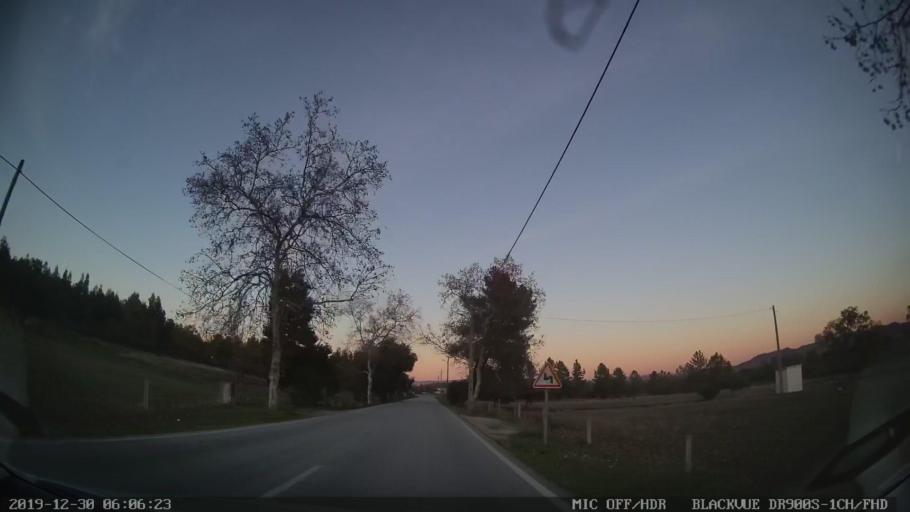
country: PT
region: Castelo Branco
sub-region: Penamacor
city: Penamacor
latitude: 40.0983
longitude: -7.2313
